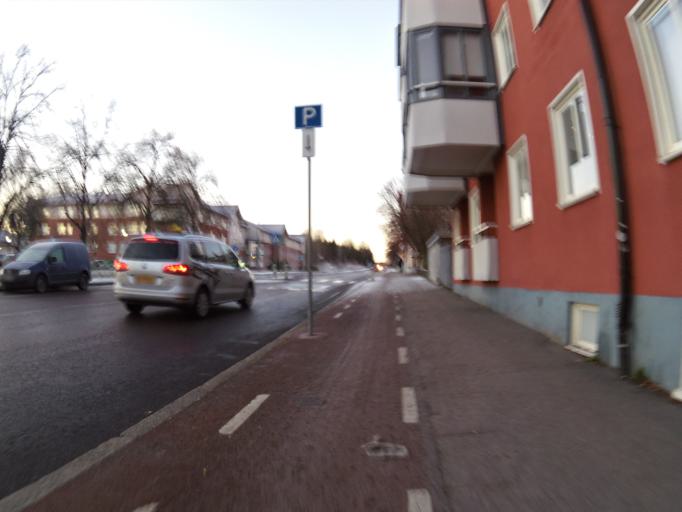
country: SE
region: Gaevleborg
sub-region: Gavle Kommun
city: Gavle
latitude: 60.6667
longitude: 17.1483
